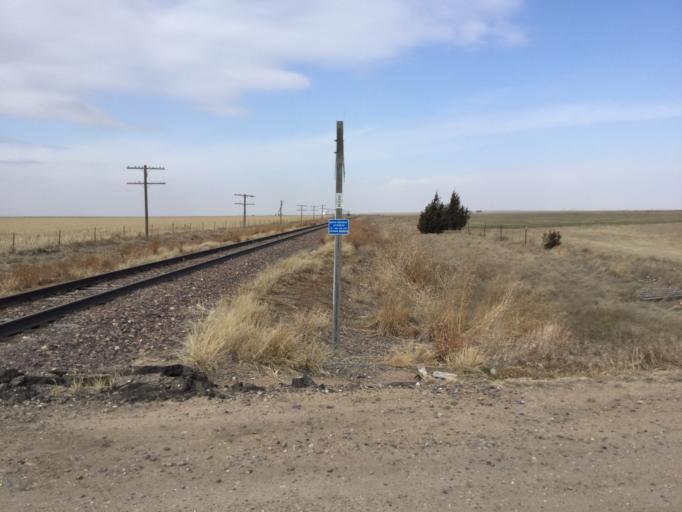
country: US
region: Kansas
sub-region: Rush County
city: La Crosse
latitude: 38.5445
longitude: -99.3646
